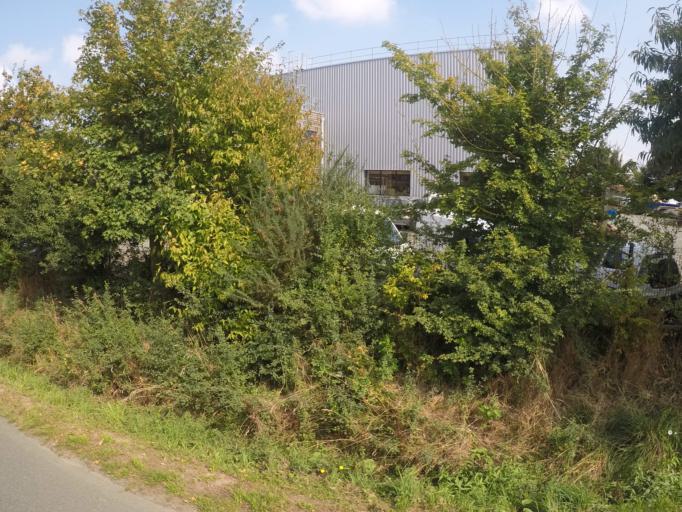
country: FR
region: Brittany
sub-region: Departement des Cotes-d'Armor
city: Tremuson
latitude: 48.5209
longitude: -2.8694
